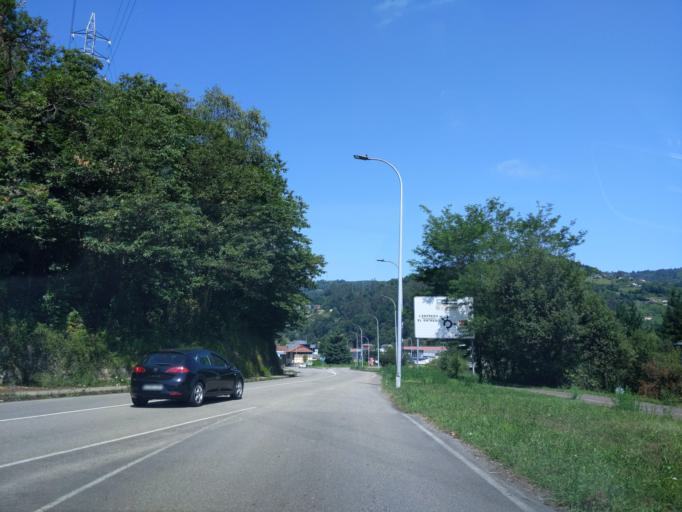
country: ES
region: Asturias
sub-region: Province of Asturias
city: El entrego
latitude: 43.2831
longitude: -5.6240
